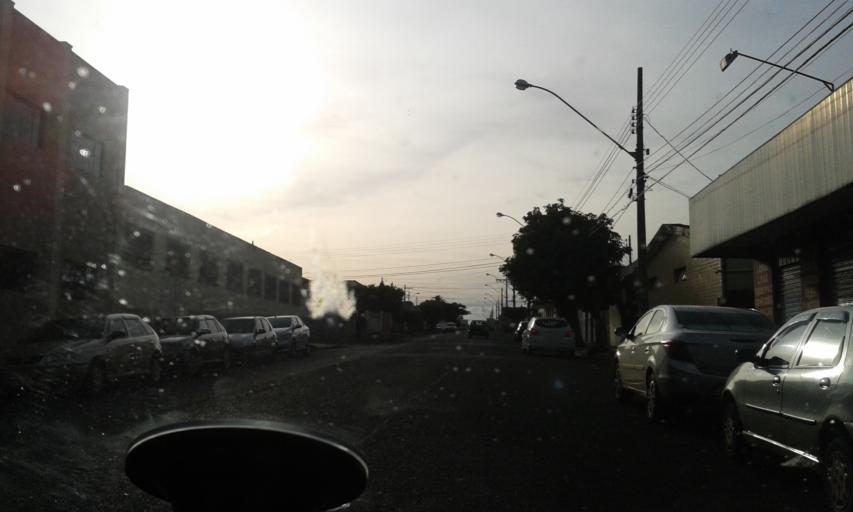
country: BR
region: Minas Gerais
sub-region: Uberlandia
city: Uberlandia
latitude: -18.9013
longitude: -48.2502
